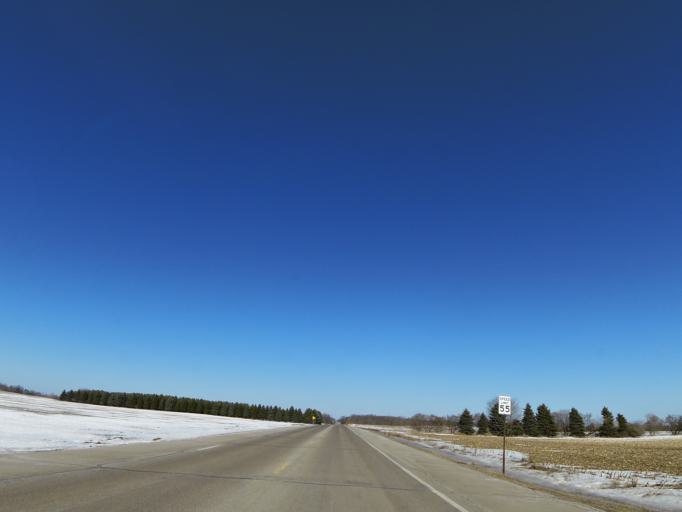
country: US
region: Minnesota
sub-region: Washington County
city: Lake Elmo
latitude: 45.0056
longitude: -92.8832
